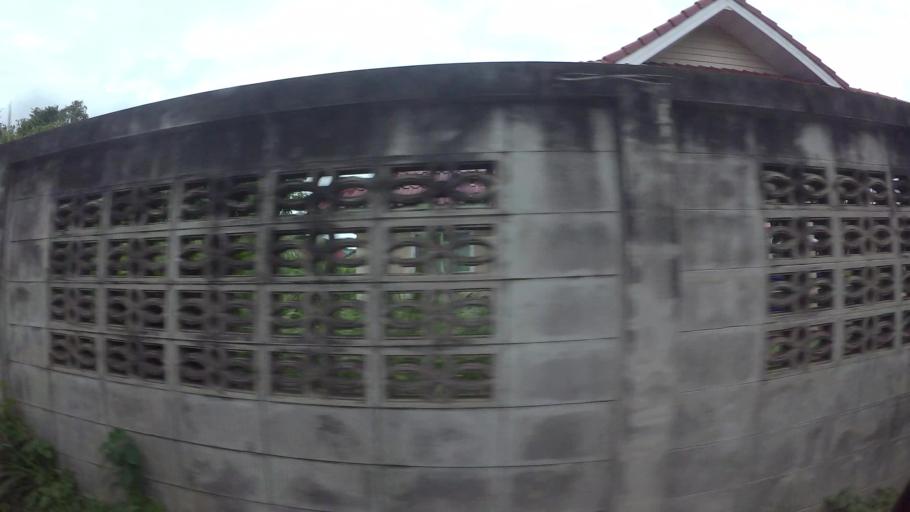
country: TH
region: Chon Buri
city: Sattahip
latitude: 12.6892
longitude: 100.9038
